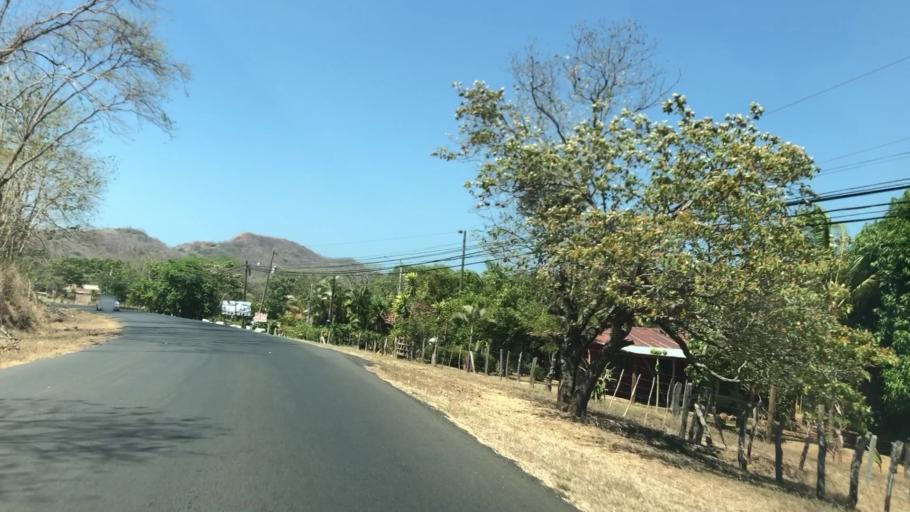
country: CR
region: Guanacaste
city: Sardinal
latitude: 10.3651
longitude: -85.8040
